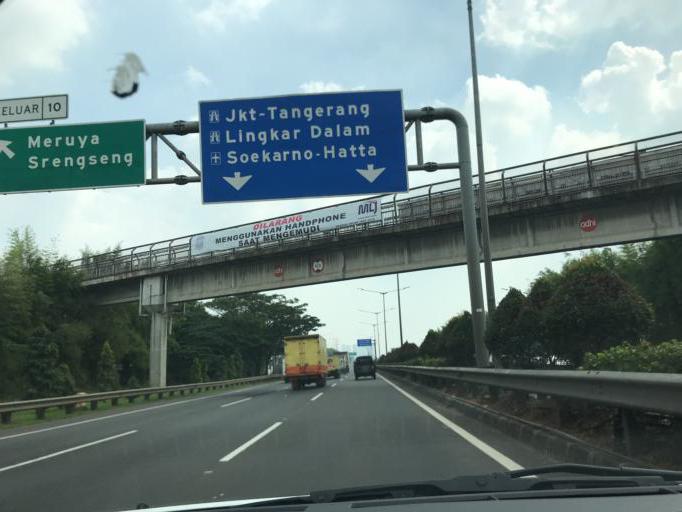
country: ID
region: West Java
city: Ciputat
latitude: -6.2119
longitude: 106.7417
